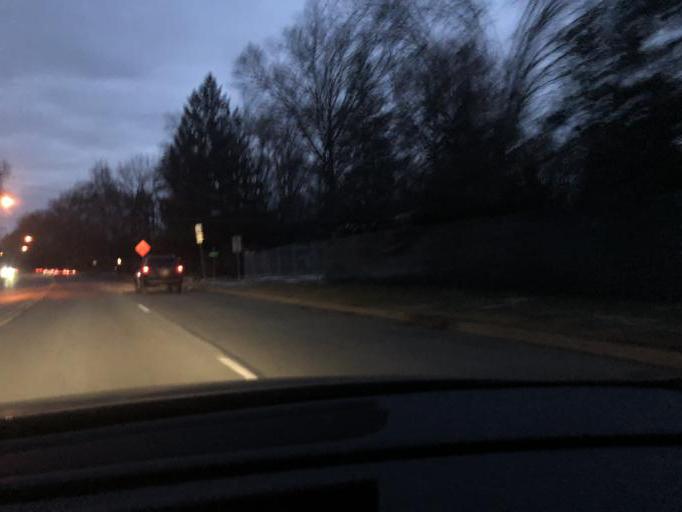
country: US
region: New Jersey
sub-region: Morris County
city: Florham Park
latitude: 40.7853
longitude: -74.3844
